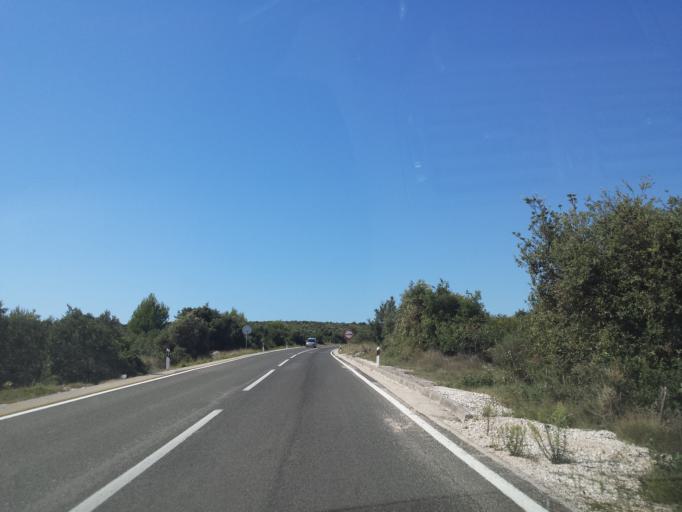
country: HR
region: Sibensko-Kniniska
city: Rogoznica
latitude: 43.5444
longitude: 15.9641
